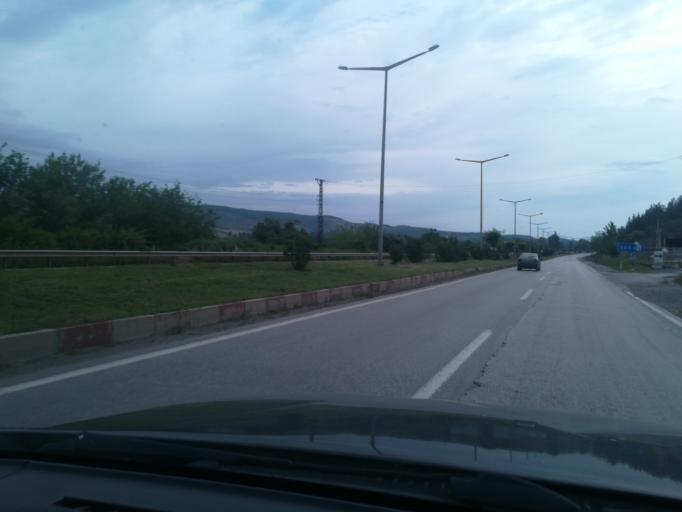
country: TR
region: Osmaniye
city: Toprakkale
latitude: 37.0541
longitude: 36.1602
